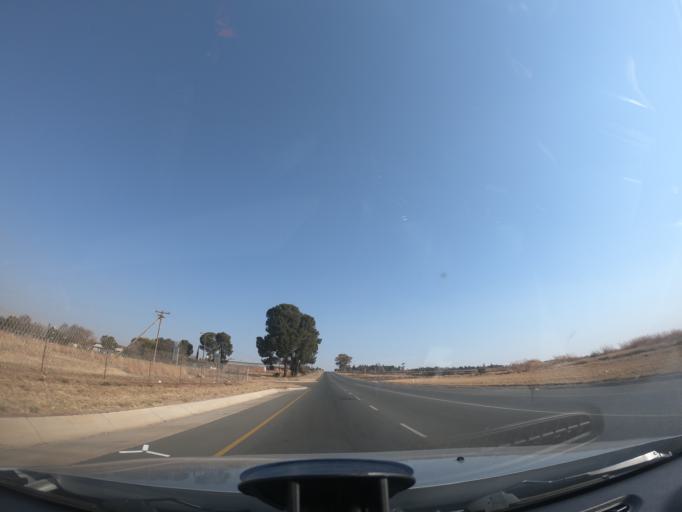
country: ZA
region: Gauteng
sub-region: City of Johannesburg Metropolitan Municipality
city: Diepsloot
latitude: -25.8622
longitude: 28.0339
